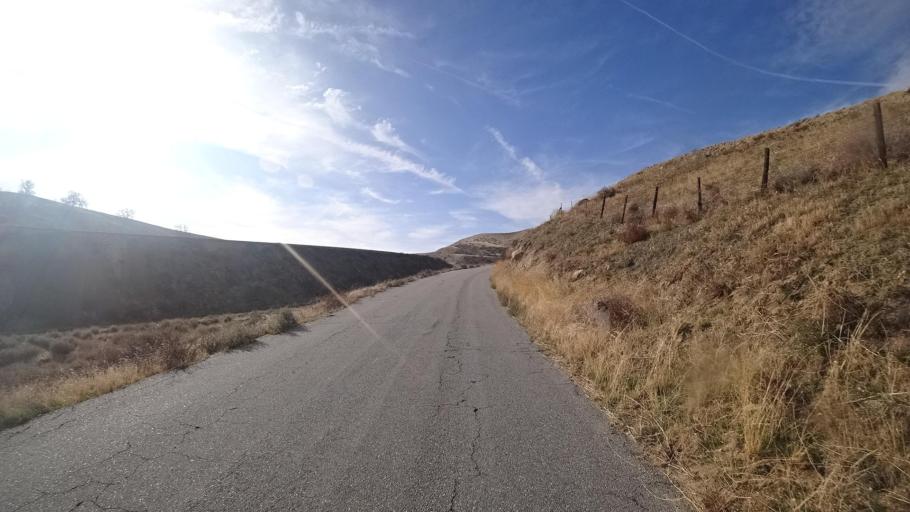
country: US
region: California
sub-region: Kern County
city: Bear Valley Springs
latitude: 35.2876
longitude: -118.6523
